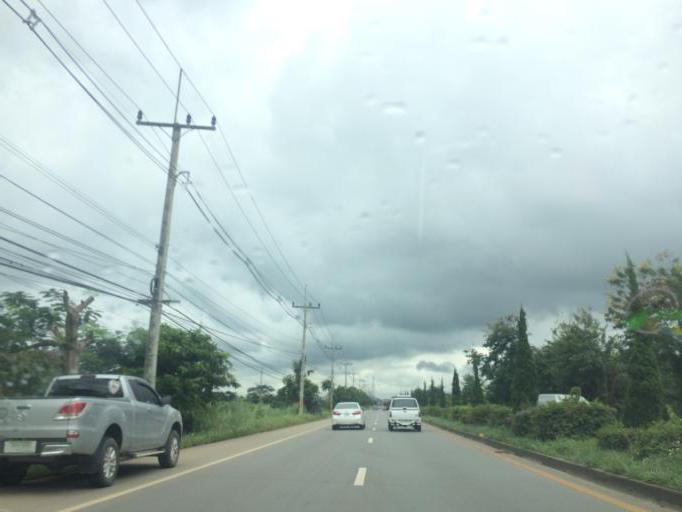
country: TH
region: Chiang Rai
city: Mae Chan
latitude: 20.0337
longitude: 99.8744
